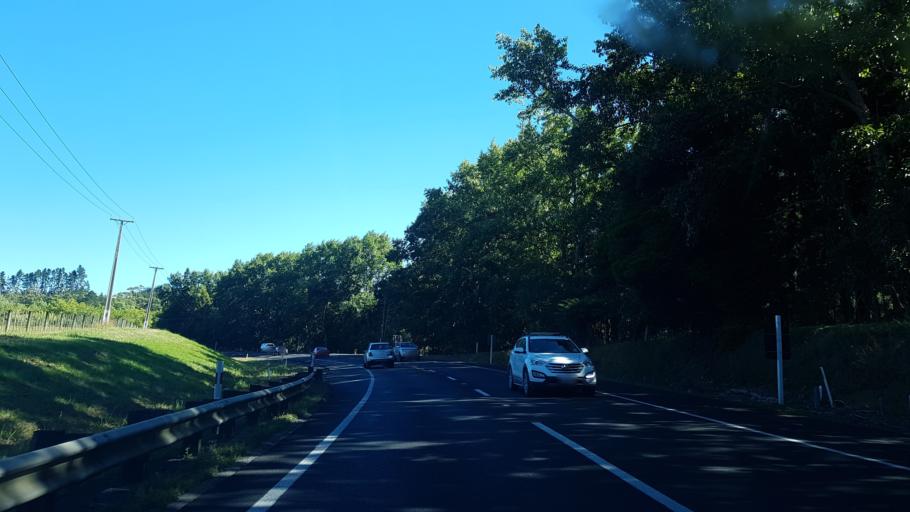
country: NZ
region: Auckland
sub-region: Auckland
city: Warkworth
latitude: -36.4353
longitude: 174.6485
